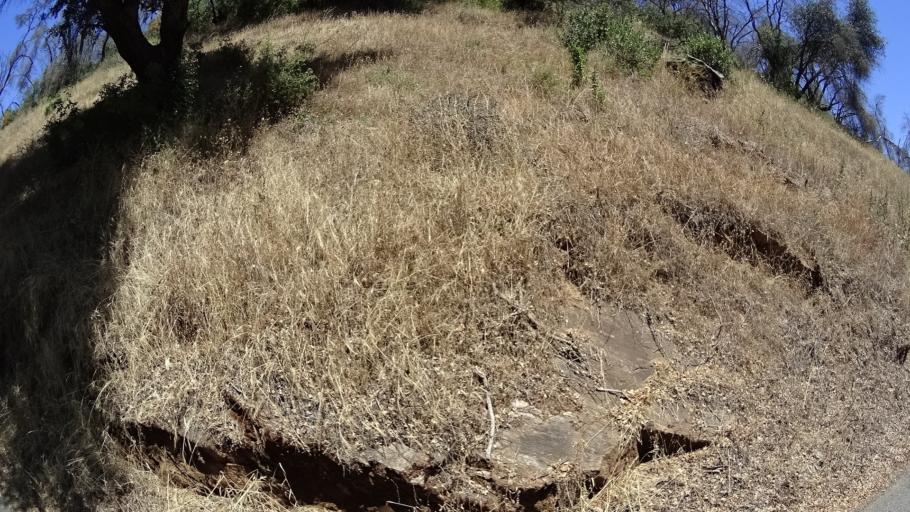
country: US
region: California
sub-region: Calaveras County
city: San Andreas
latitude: 38.2860
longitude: -120.6595
